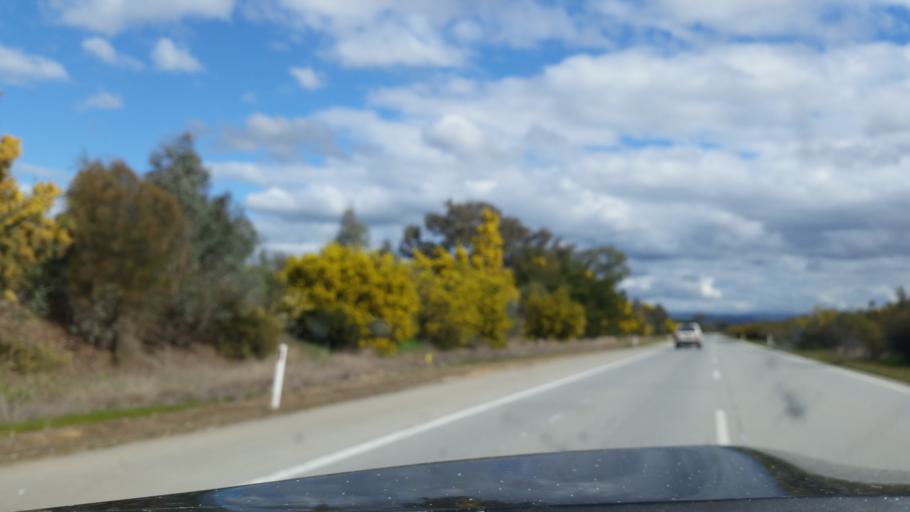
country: AU
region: New South Wales
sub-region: Albury Municipality
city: Lavington
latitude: -36.0112
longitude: 146.9880
